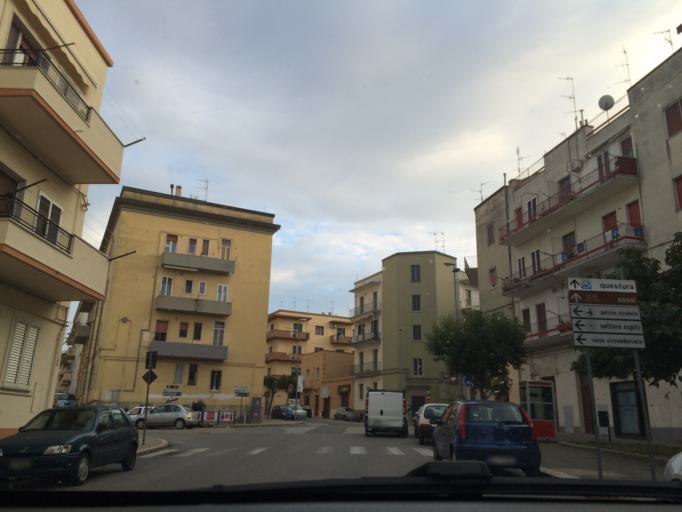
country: IT
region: Basilicate
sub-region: Provincia di Matera
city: Matera
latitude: 40.6755
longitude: 16.5996
